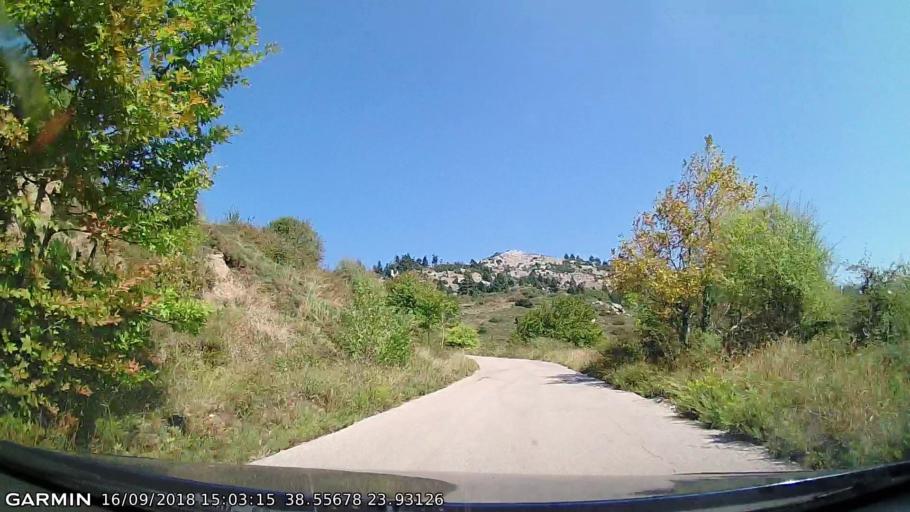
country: GR
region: Central Greece
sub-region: Nomos Evvoias
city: Yimnon
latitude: 38.5567
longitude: 23.9315
